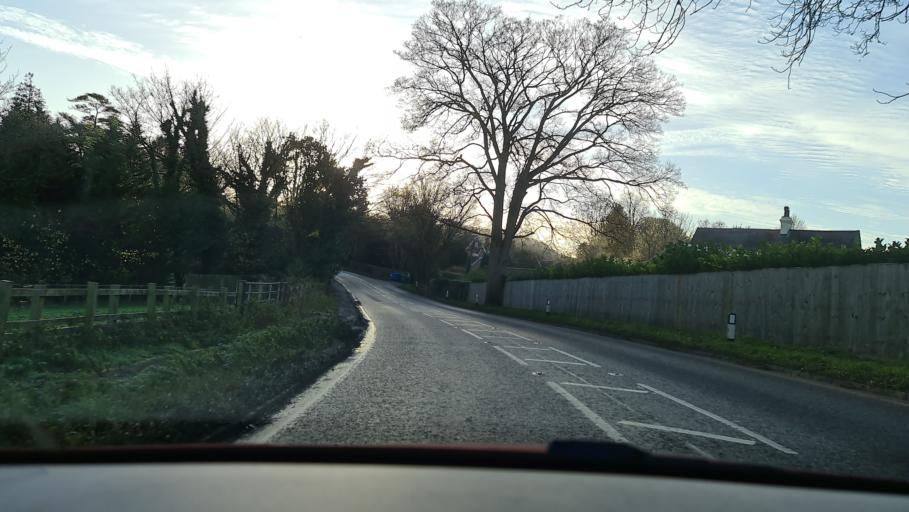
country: GB
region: England
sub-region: Buckinghamshire
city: Princes Risborough
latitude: 51.7519
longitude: -0.8080
